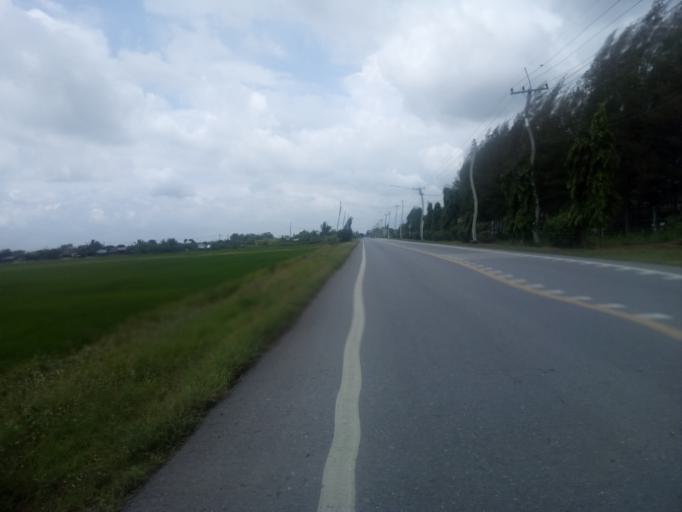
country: TH
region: Pathum Thani
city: Ban Lam Luk Ka
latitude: 14.0094
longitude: 100.8228
